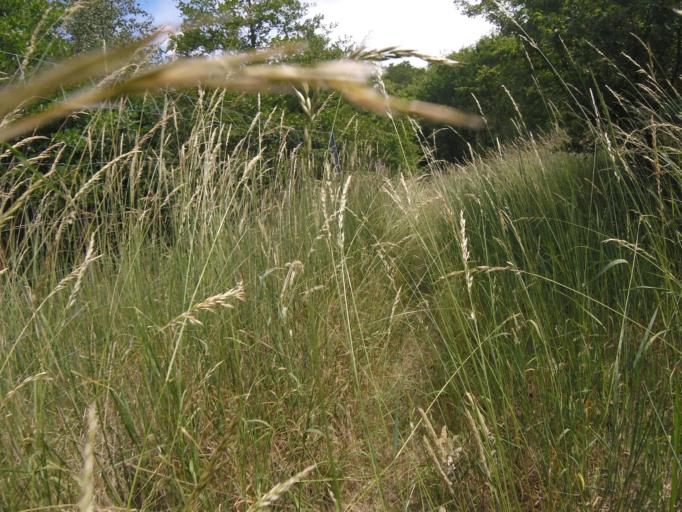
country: DE
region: Brandenburg
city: Konigs Wusterhausen
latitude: 52.3082
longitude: 13.6236
